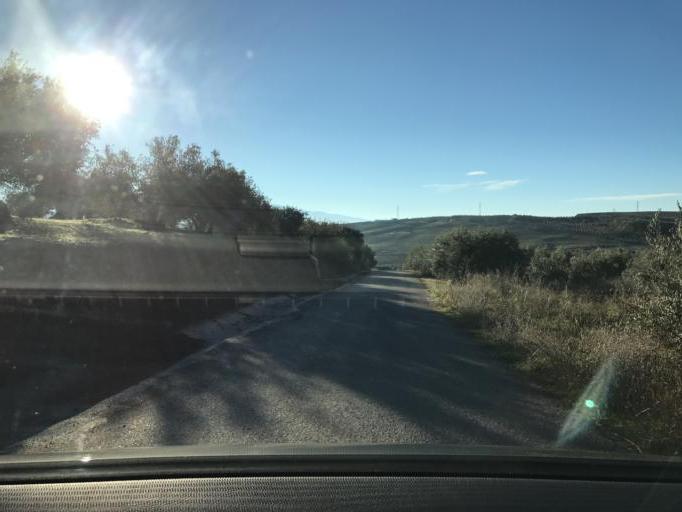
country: ES
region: Andalusia
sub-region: Provincia de Granada
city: Calicasas
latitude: 37.2770
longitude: -3.6199
